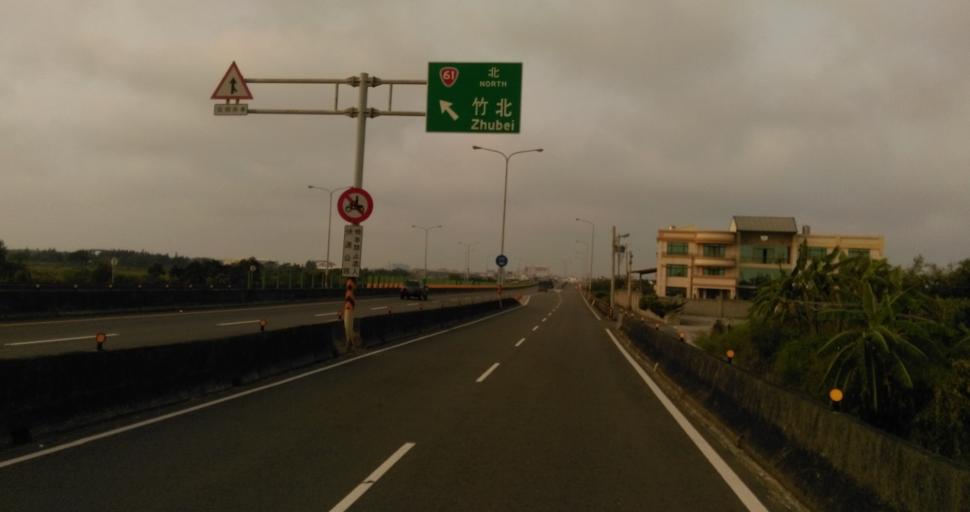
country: TW
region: Taiwan
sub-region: Hsinchu
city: Hsinchu
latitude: 24.7948
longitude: 120.9198
